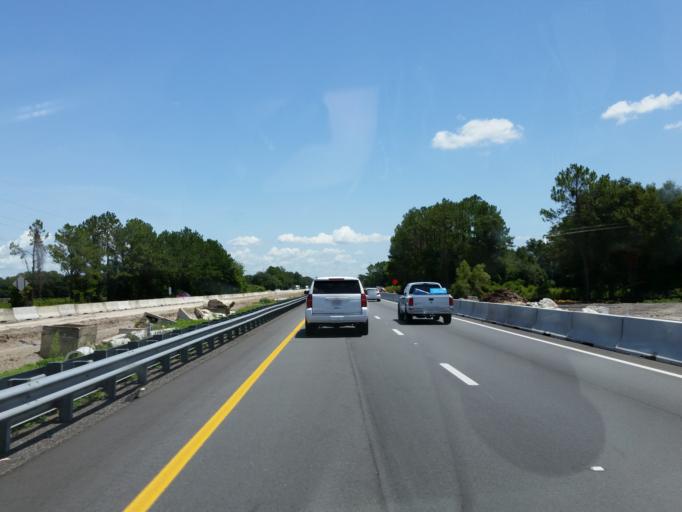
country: US
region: Florida
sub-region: Sumter County
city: Bushnell
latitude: 28.6879
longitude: -82.1320
